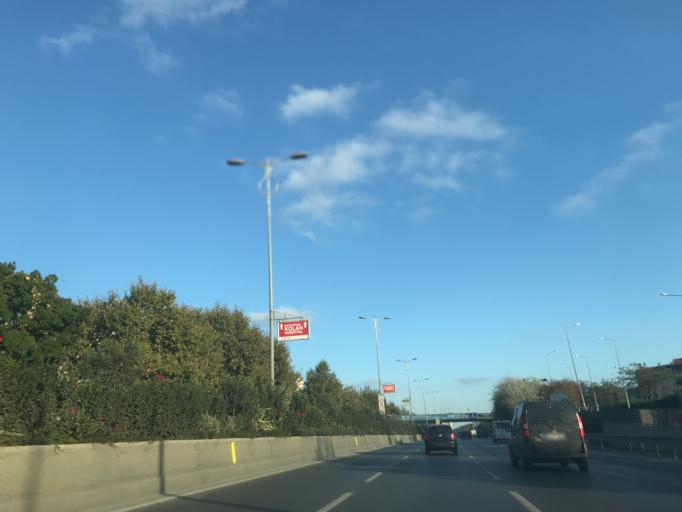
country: TR
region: Istanbul
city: Esenler
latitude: 41.0509
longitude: 28.8718
